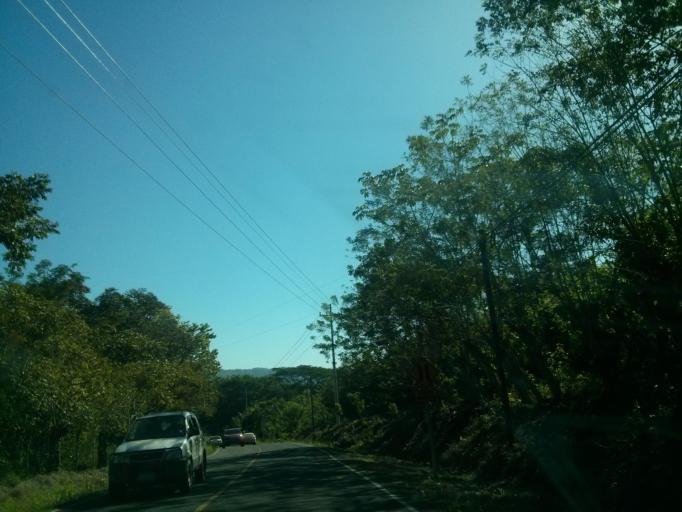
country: CR
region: Puntarenas
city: Paquera
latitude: 9.7339
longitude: -85.0248
